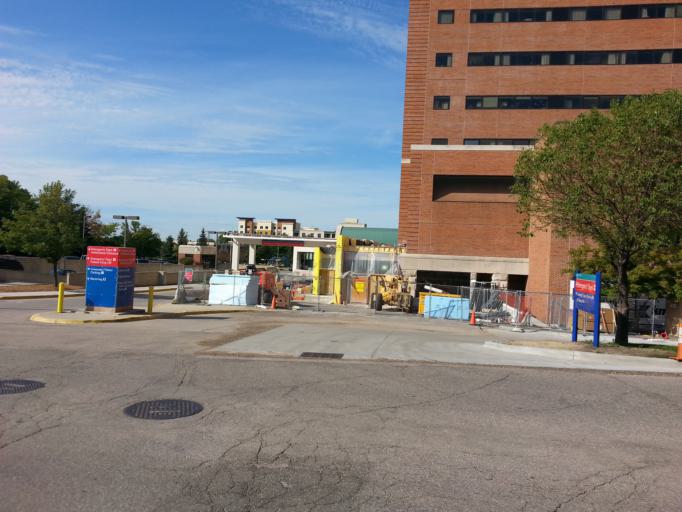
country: US
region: Minnesota
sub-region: Olmsted County
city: Rochester
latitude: 44.0192
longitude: -92.4831
